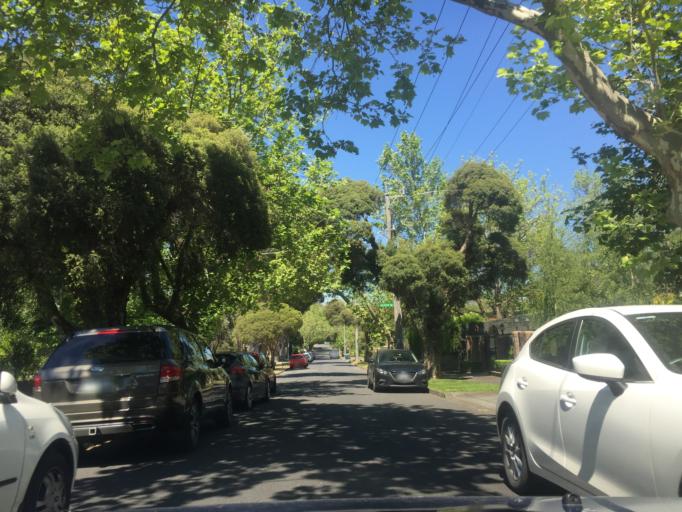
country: AU
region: Victoria
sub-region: Boroondara
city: Canterbury
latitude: -37.8211
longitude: 145.0868
